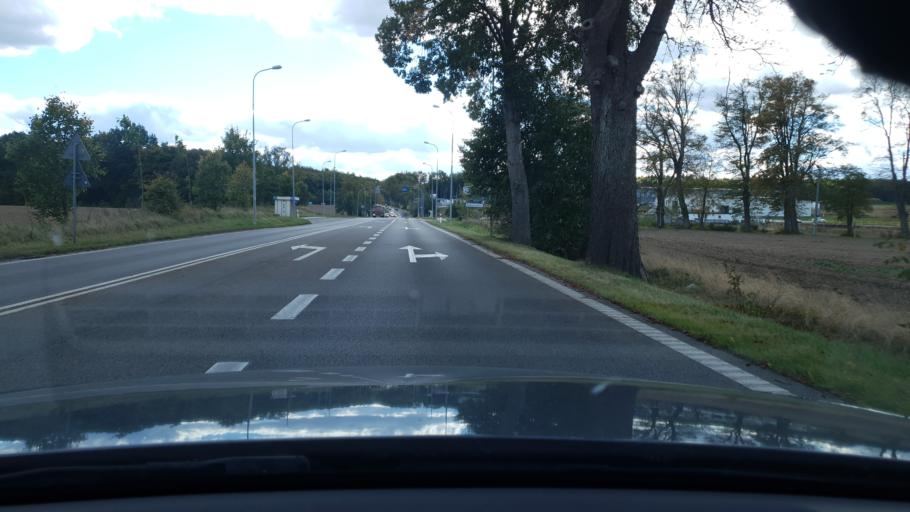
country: PL
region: Pomeranian Voivodeship
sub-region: Powiat wejherowski
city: Rekowo Dolne
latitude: 54.6391
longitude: 18.3460
